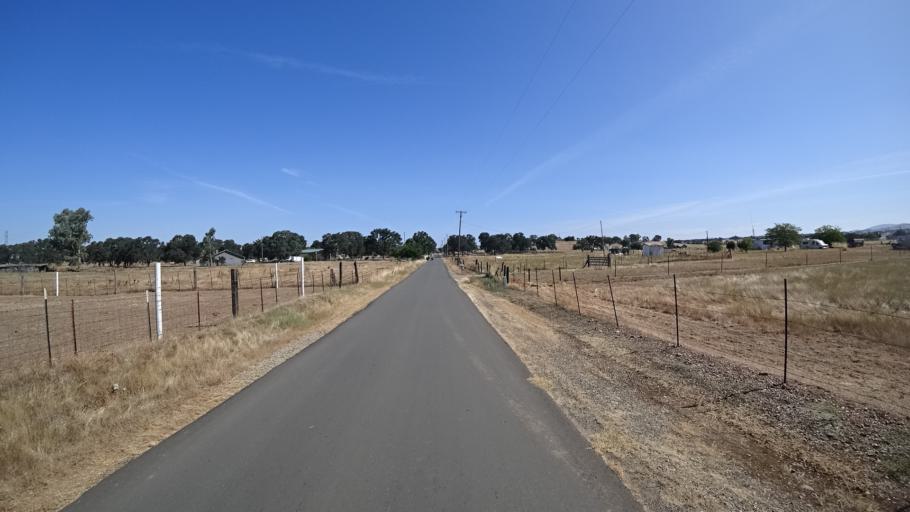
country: US
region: California
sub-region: Calaveras County
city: Rancho Calaveras
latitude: 38.0932
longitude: -120.9084
